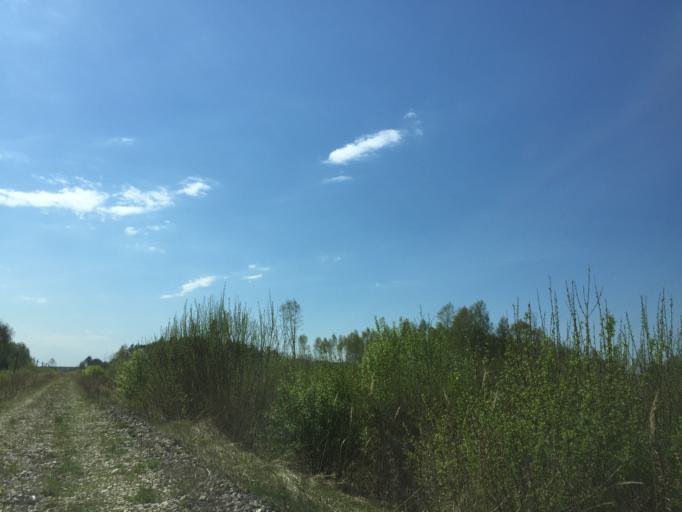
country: LV
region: Saulkrastu
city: Saulkrasti
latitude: 57.3457
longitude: 24.4840
